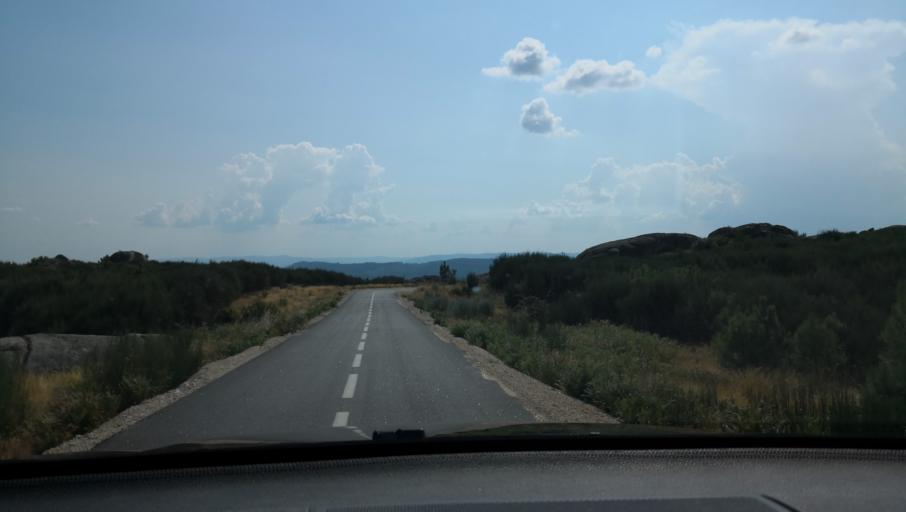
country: PT
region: Vila Real
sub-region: Sabrosa
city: Sabrosa
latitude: 41.2855
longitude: -7.6133
